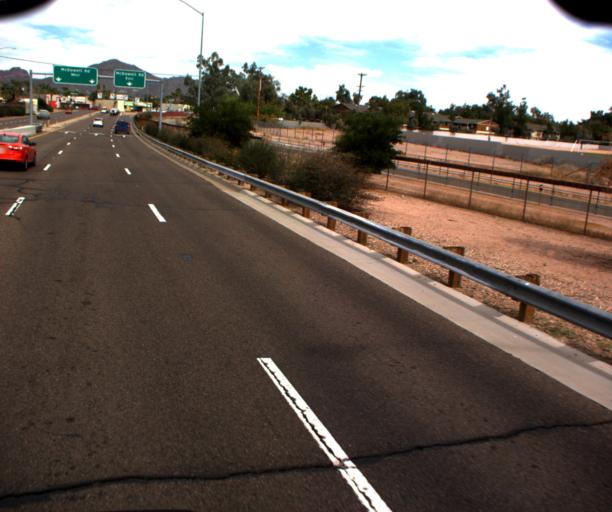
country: US
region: Arizona
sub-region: Maricopa County
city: Tempe Junction
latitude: 33.4631
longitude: -111.9826
